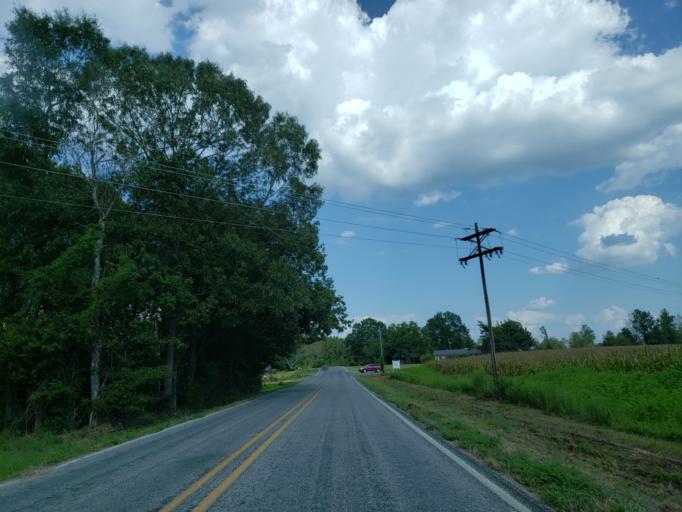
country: US
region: Mississippi
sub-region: Covington County
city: Collins
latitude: 31.6194
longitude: -89.3909
